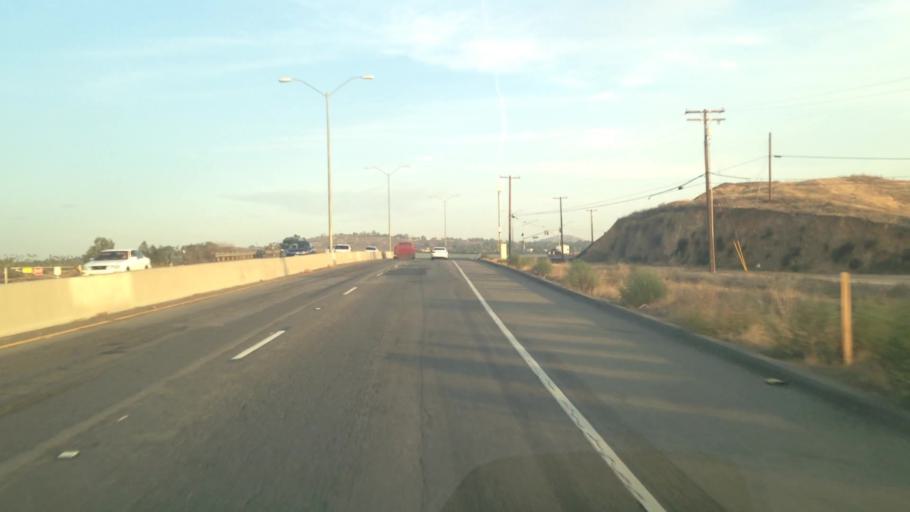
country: US
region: California
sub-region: Riverside County
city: Riverside
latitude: 33.8939
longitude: -117.4220
